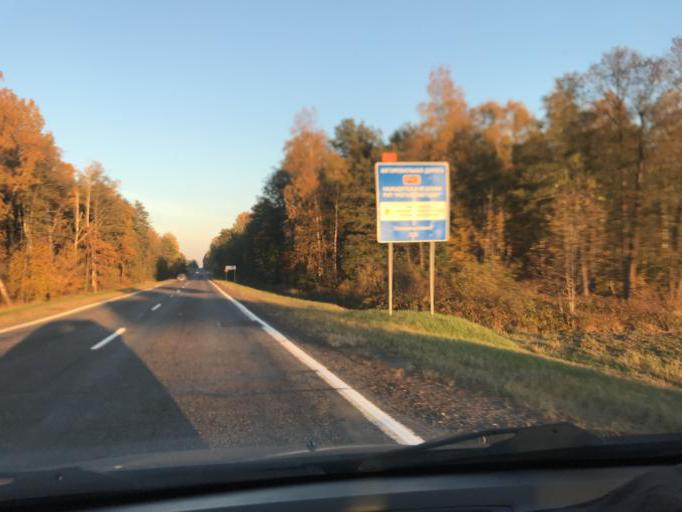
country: BY
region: Mogilev
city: Hlusk
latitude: 53.0649
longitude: 28.5346
